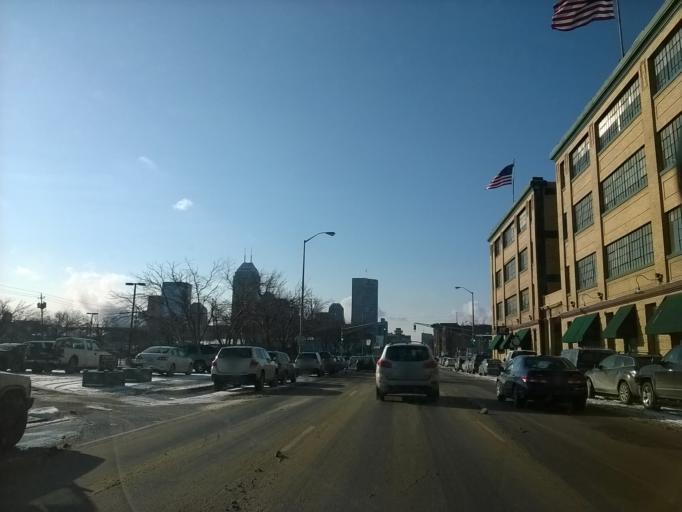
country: US
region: Indiana
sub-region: Marion County
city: Indianapolis
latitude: 39.7818
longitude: -86.1612
